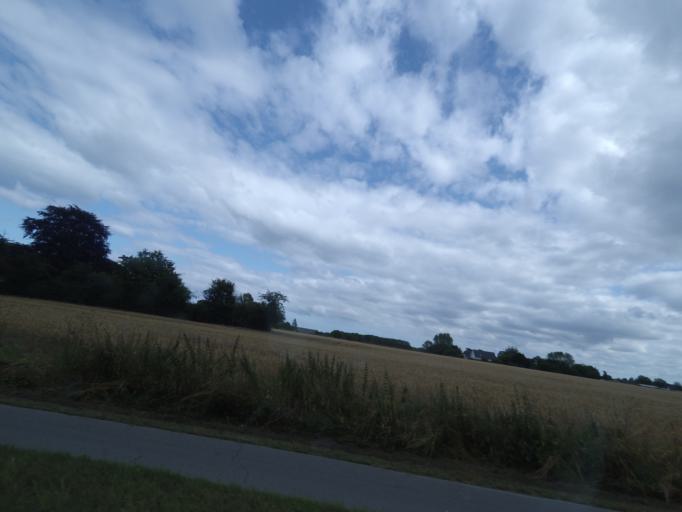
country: DK
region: South Denmark
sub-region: Nordfyns Kommune
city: Otterup
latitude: 55.5493
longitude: 10.4415
